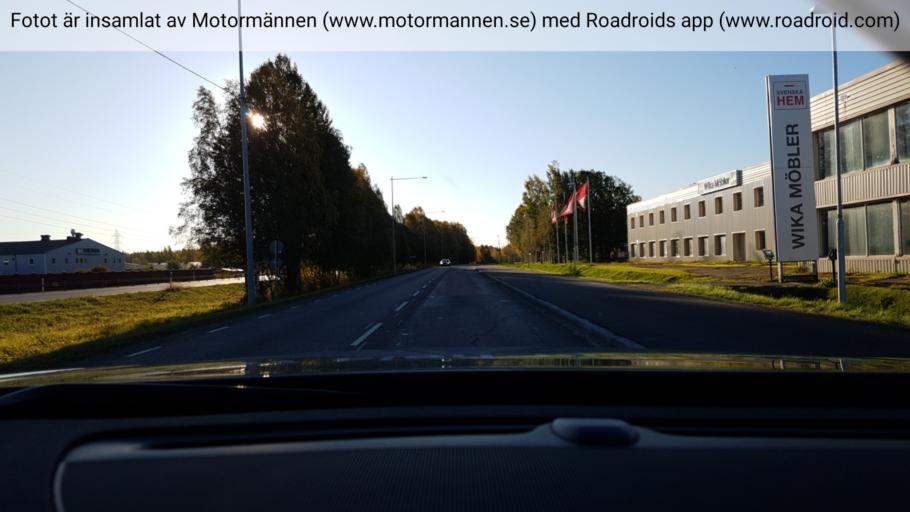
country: SE
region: Norrbotten
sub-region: Lulea Kommun
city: Gammelstad
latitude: 65.6405
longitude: 22.0187
